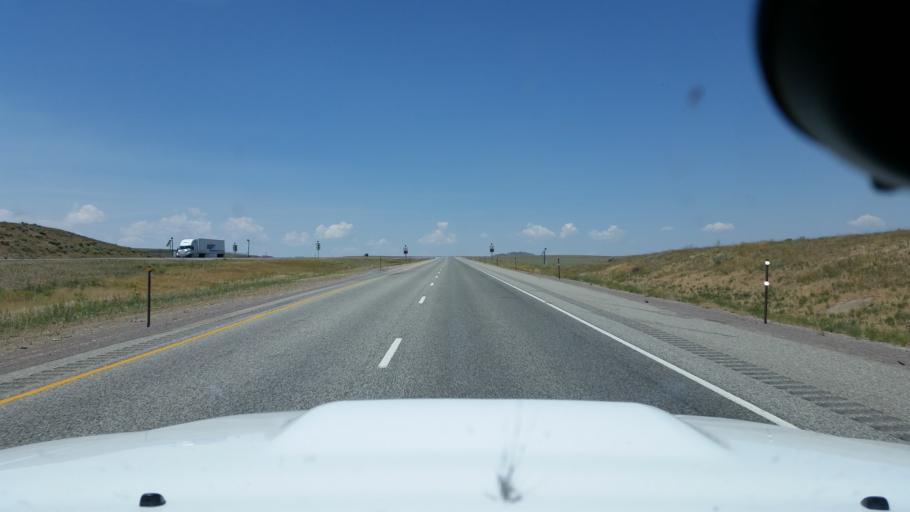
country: US
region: Wyoming
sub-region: Carbon County
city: Saratoga
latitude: 41.7382
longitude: -106.6103
